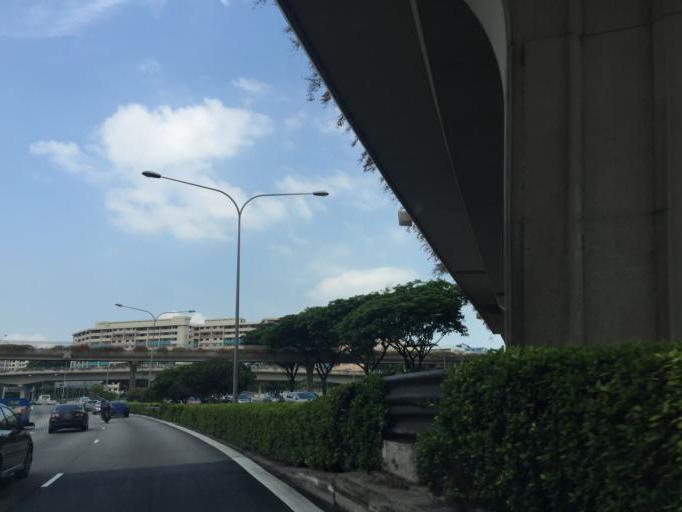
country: SG
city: Singapore
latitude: 1.3210
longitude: 103.8749
